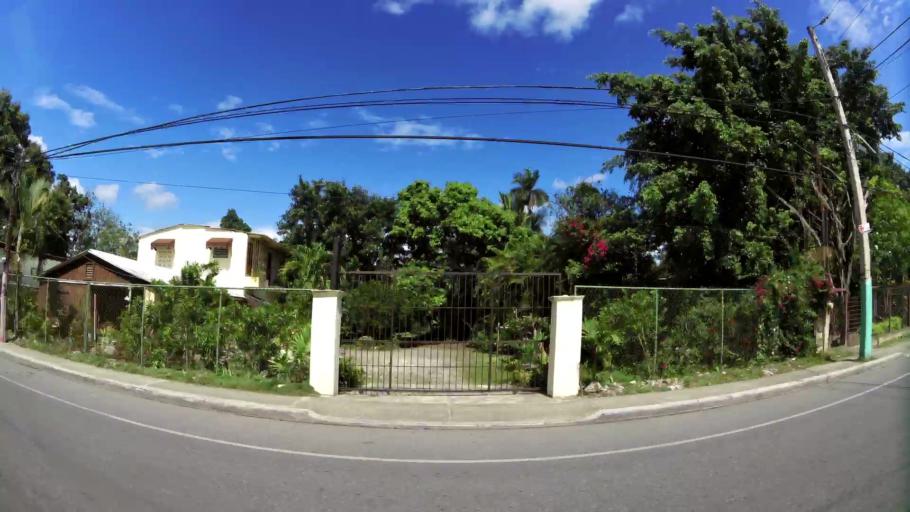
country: DO
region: La Vega
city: Concepcion de La Vega
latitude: 19.2419
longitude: -70.5366
